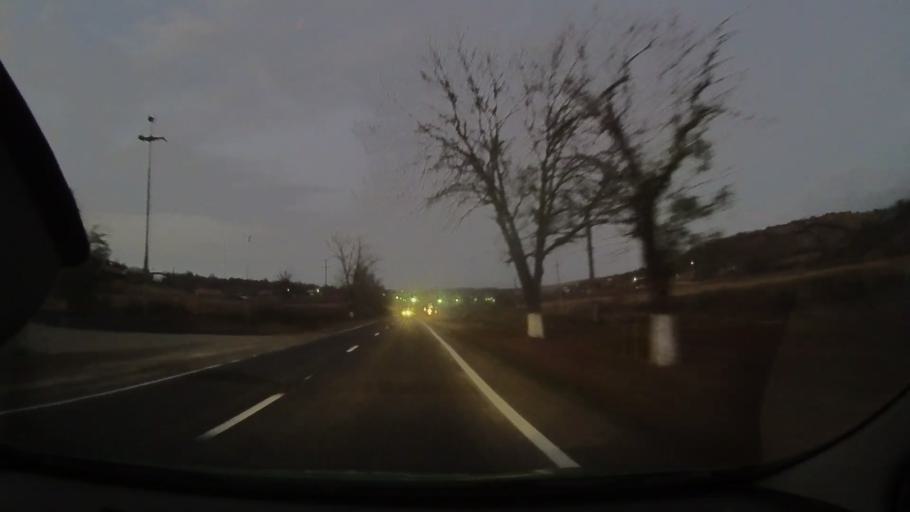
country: RO
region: Constanta
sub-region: Comuna Ion Corvin
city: Ion Corvin
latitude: 44.1070
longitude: 27.8013
